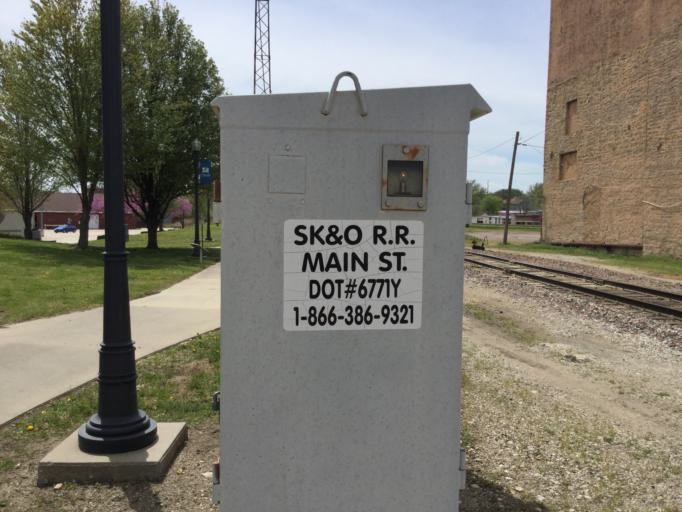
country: US
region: Kansas
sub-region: Neosho County
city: Chanute
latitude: 37.6816
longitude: -95.4532
